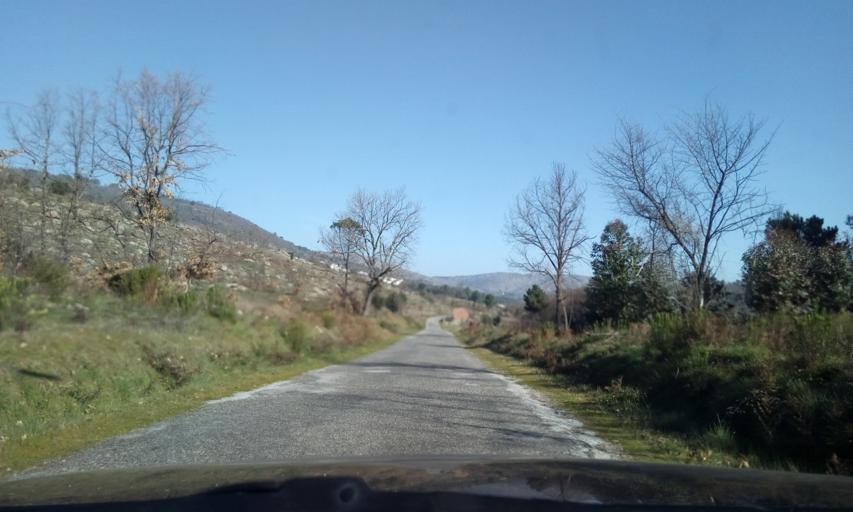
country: PT
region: Guarda
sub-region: Celorico da Beira
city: Celorico da Beira
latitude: 40.6719
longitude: -7.4567
